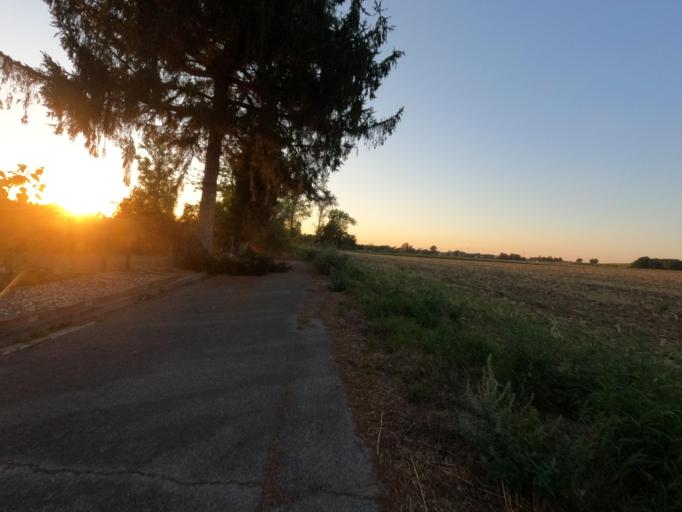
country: DE
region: North Rhine-Westphalia
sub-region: Regierungsbezirk Koln
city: Linnich
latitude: 50.9646
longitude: 6.3114
